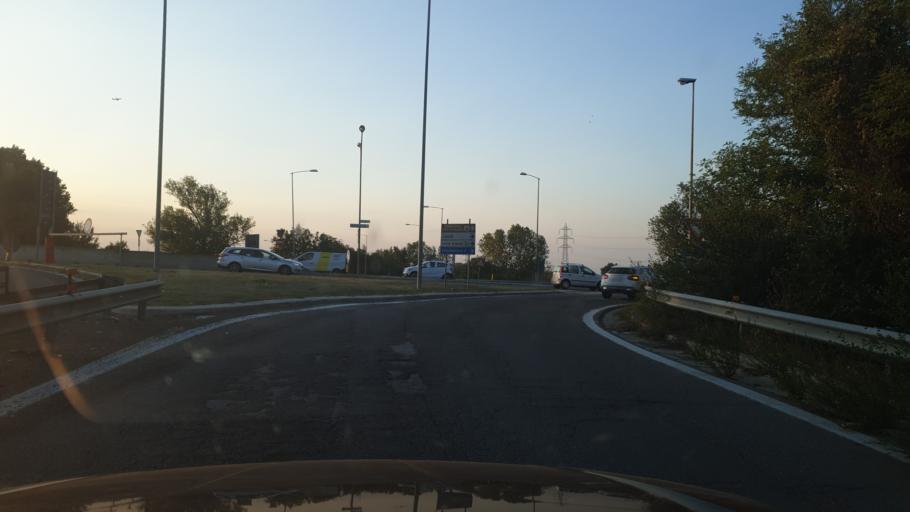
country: IT
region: Emilia-Romagna
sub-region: Provincia di Bologna
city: Quarto Inferiore
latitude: 44.5150
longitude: 11.3789
